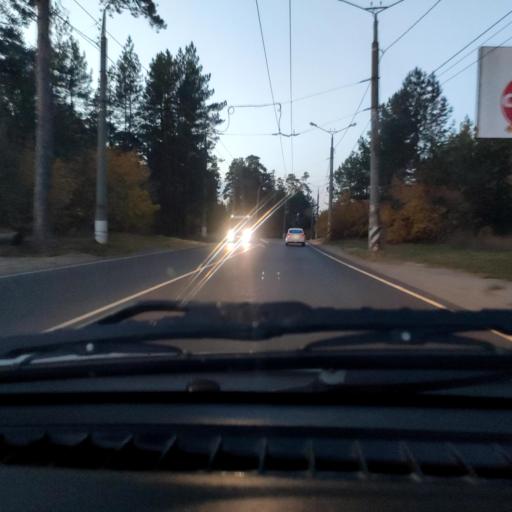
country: RU
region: Samara
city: Tol'yatti
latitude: 53.4787
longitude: 49.3499
